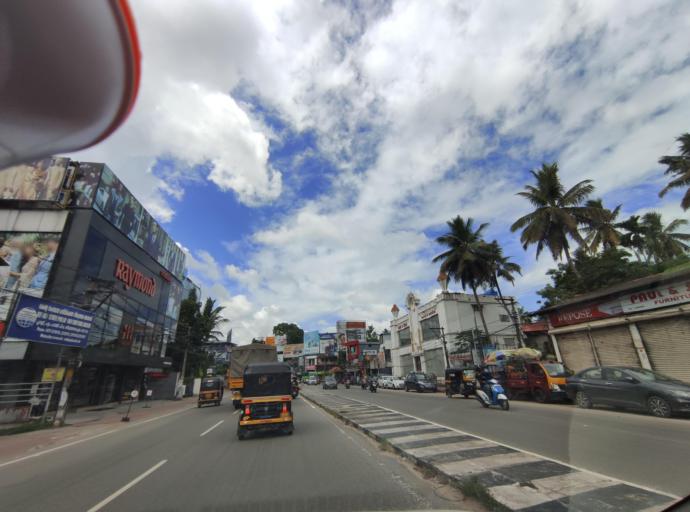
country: IN
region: Kerala
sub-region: Thiruvananthapuram
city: Thiruvananthapuram
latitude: 8.5142
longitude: 76.9455
